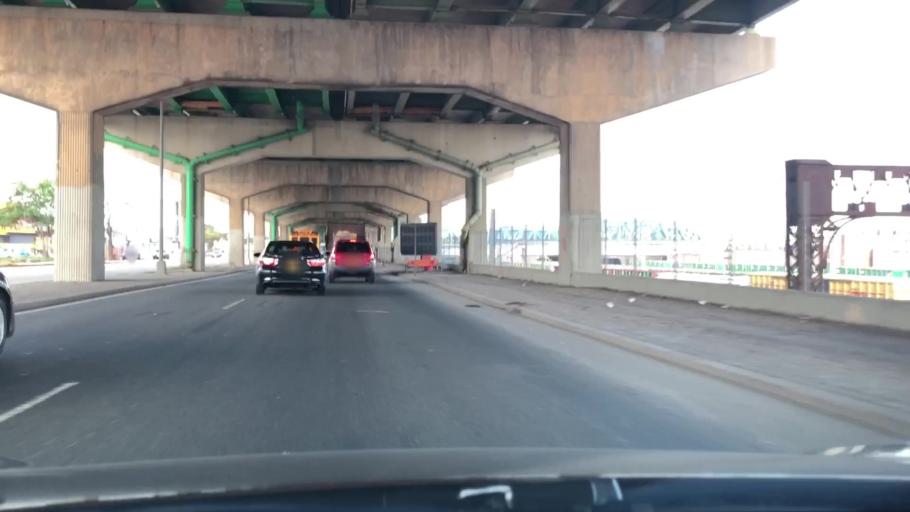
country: US
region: New York
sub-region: Bronx
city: The Bronx
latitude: 40.8115
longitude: -73.8998
